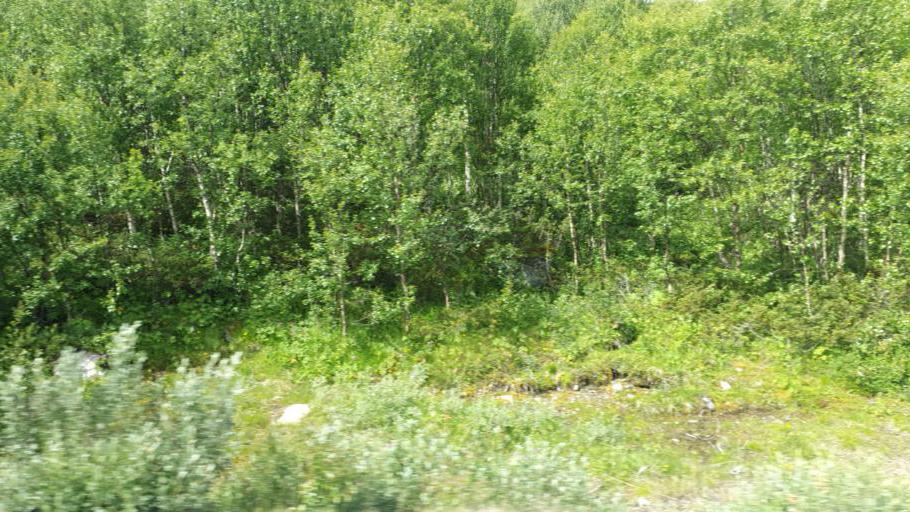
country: NO
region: Oppland
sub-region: Vaga
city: Vagamo
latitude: 61.5305
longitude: 8.8793
